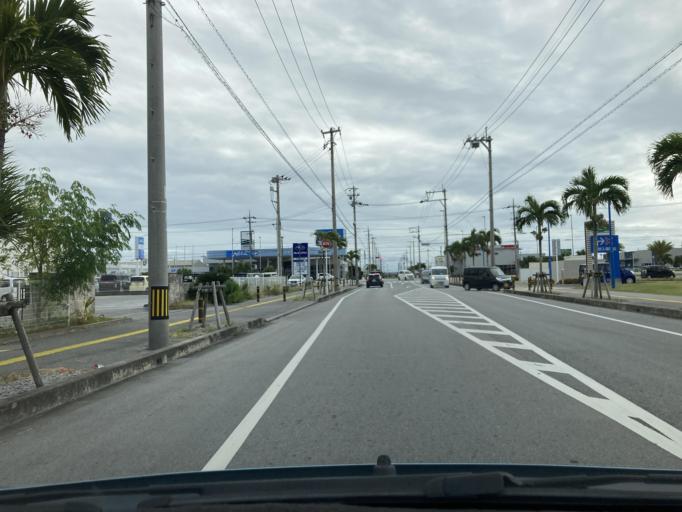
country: JP
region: Okinawa
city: Itoman
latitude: 26.1572
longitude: 127.6527
